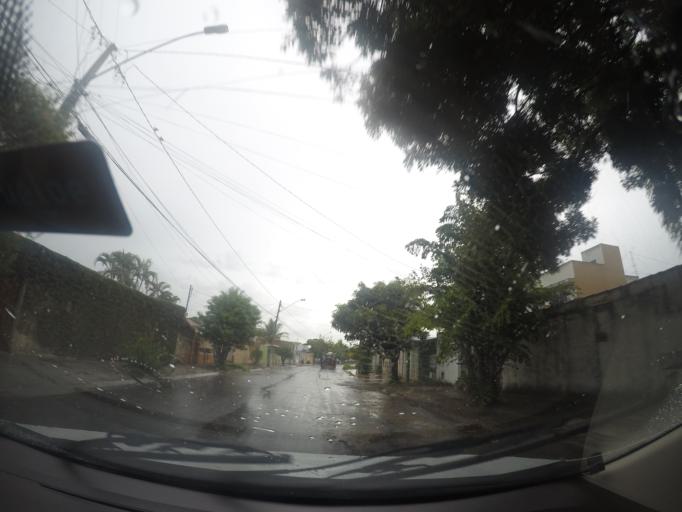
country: BR
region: Goias
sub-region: Goiania
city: Goiania
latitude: -16.6462
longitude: -49.2238
